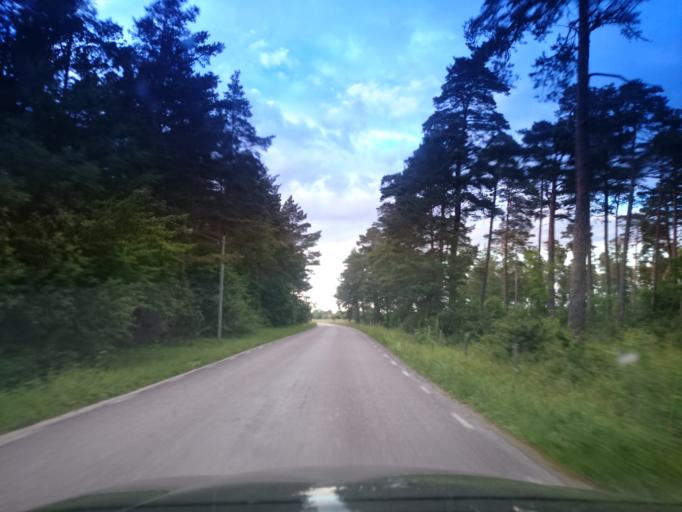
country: SE
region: Gotland
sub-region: Gotland
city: Visby
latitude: 57.5391
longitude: 18.3901
